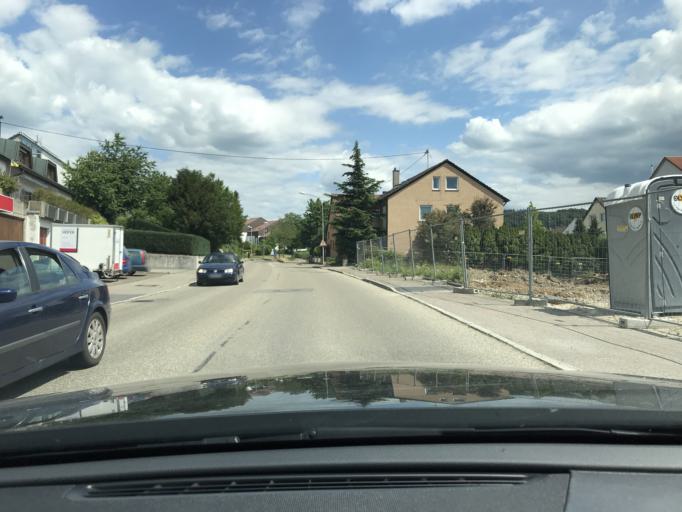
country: DE
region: Baden-Wuerttemberg
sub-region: Regierungsbezirk Stuttgart
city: Schwaikheim
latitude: 48.8740
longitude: 9.3564
